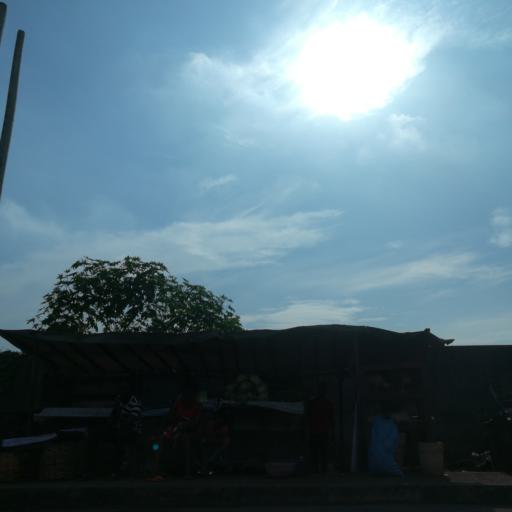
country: NG
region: Rivers
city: Port Harcourt
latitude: 4.8050
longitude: 7.0249
